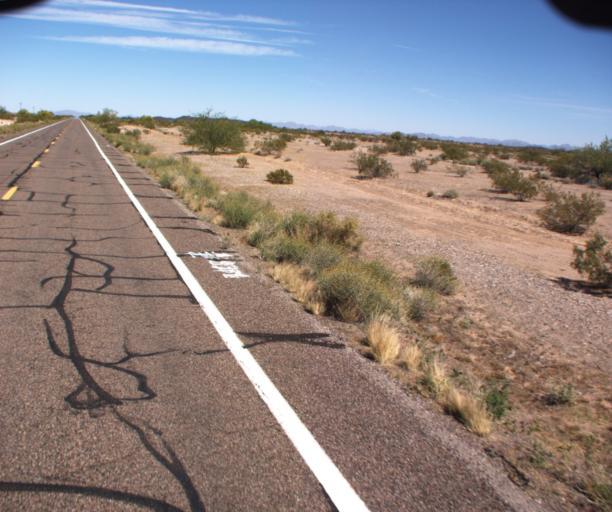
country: US
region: Arizona
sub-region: Maricopa County
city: Gila Bend
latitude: 32.7825
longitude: -112.8093
